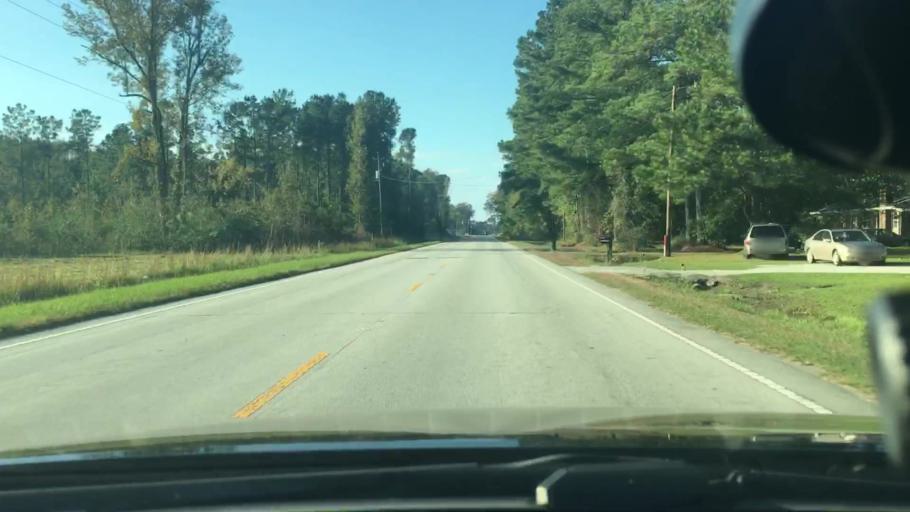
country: US
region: North Carolina
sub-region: Craven County
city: Vanceboro
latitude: 35.3459
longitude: -77.1828
